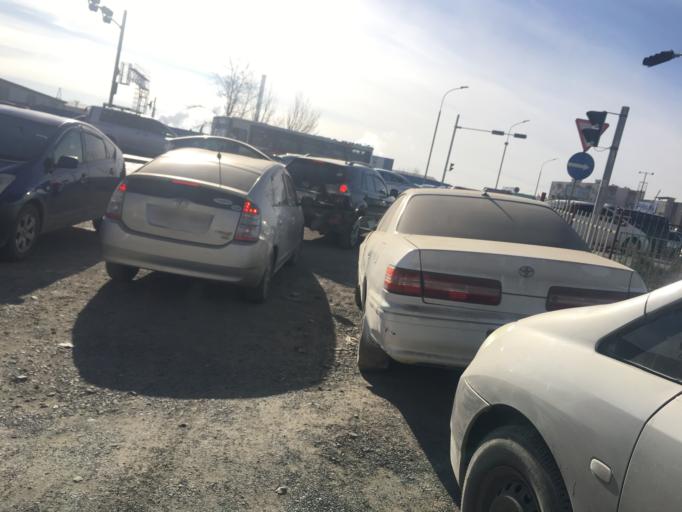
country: MN
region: Ulaanbaatar
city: Ulaanbaatar
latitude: 47.9099
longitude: 106.8023
